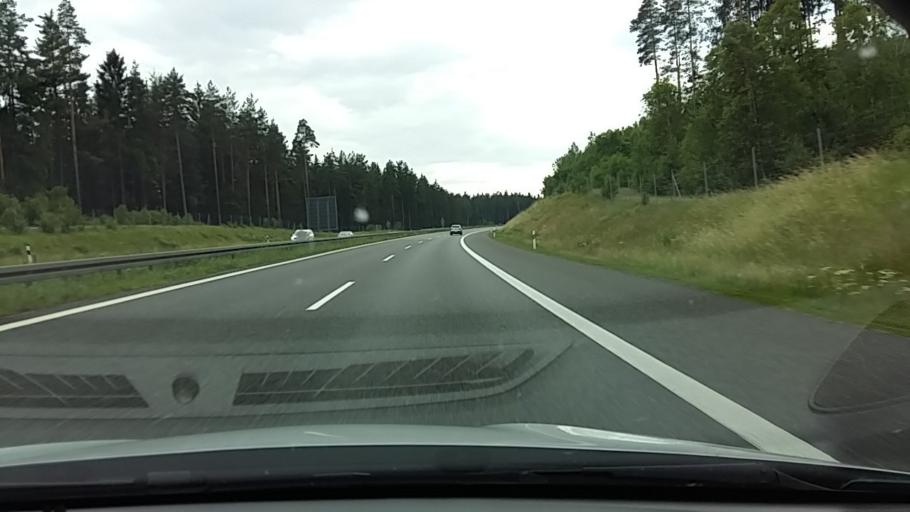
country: DE
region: Bavaria
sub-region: Upper Palatinate
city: Moosbach
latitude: 49.6149
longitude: 12.4105
